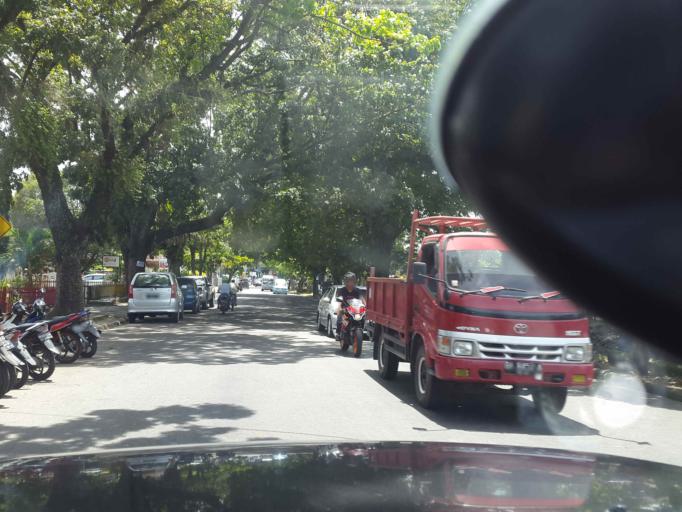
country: ID
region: West Sumatra
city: Padang
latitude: -0.9388
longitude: 100.3661
